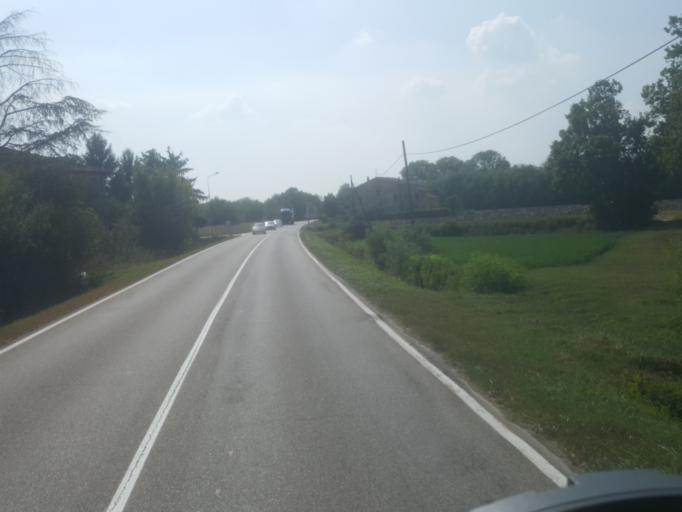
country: IT
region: Lombardy
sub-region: Provincia di Cremona
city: Casalmaggiore
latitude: 44.9636
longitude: 10.3980
